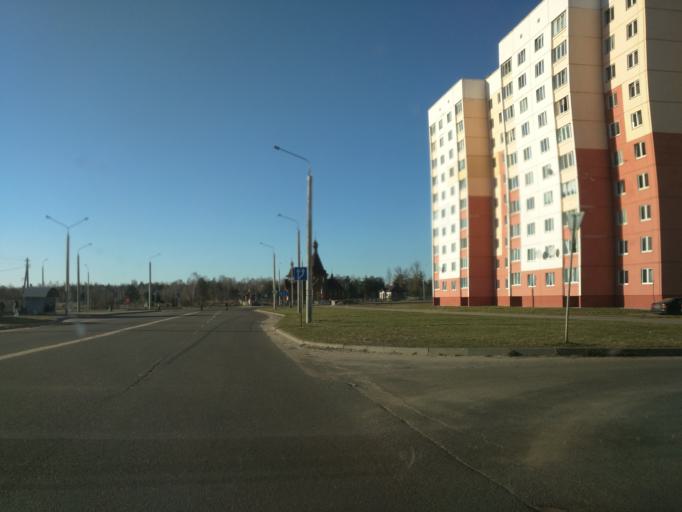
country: BY
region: Mogilev
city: Babruysk
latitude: 53.1664
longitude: 29.1644
